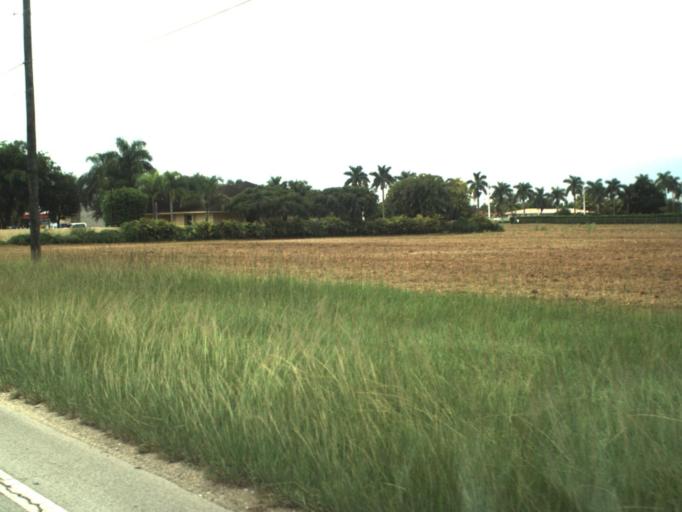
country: US
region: Florida
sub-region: Miami-Dade County
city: Naranja
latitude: 25.5375
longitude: -80.4781
